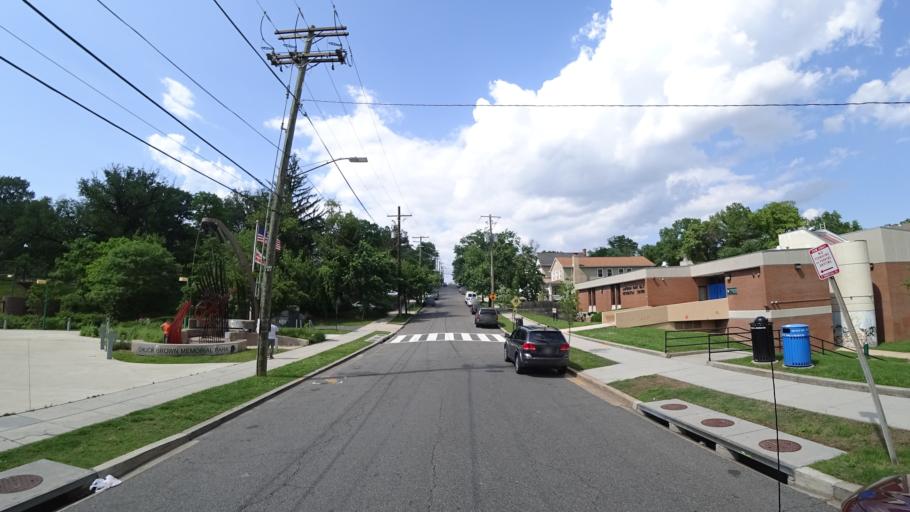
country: US
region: Maryland
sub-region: Prince George's County
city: Mount Rainier
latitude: 38.9264
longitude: -76.9762
